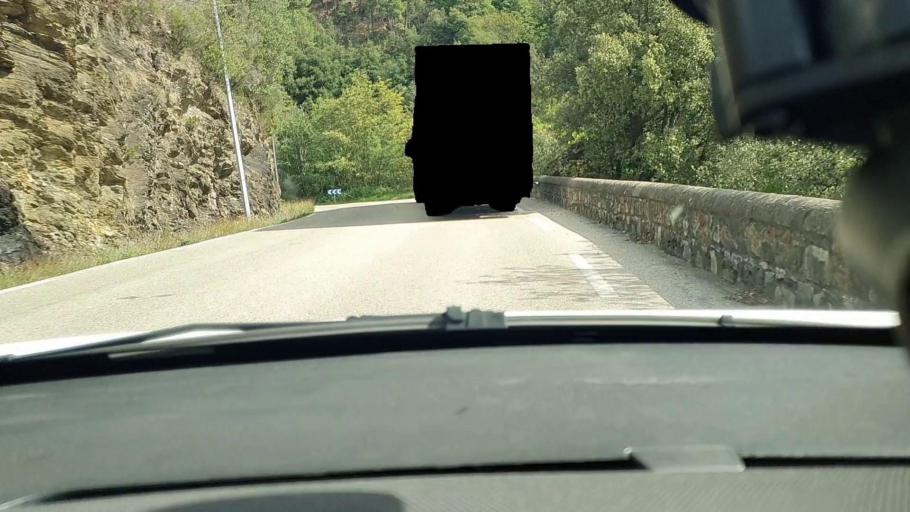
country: FR
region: Languedoc-Roussillon
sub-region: Departement du Gard
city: Laval-Pradel
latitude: 44.2513
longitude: 4.0641
